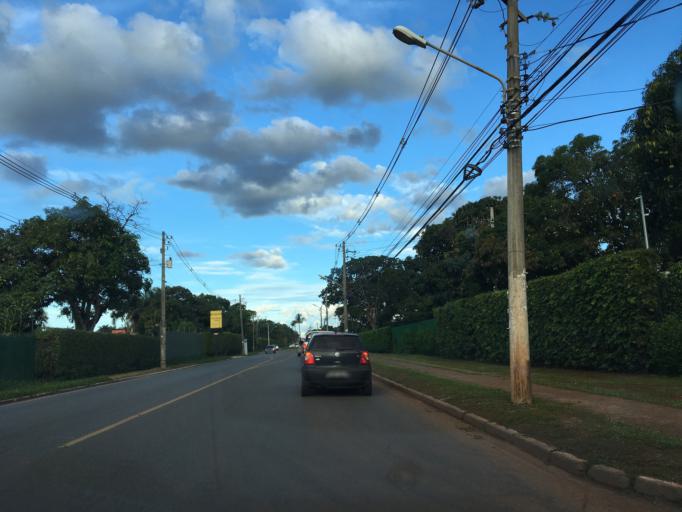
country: BR
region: Federal District
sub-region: Brasilia
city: Brasilia
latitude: -15.8473
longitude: -47.8889
